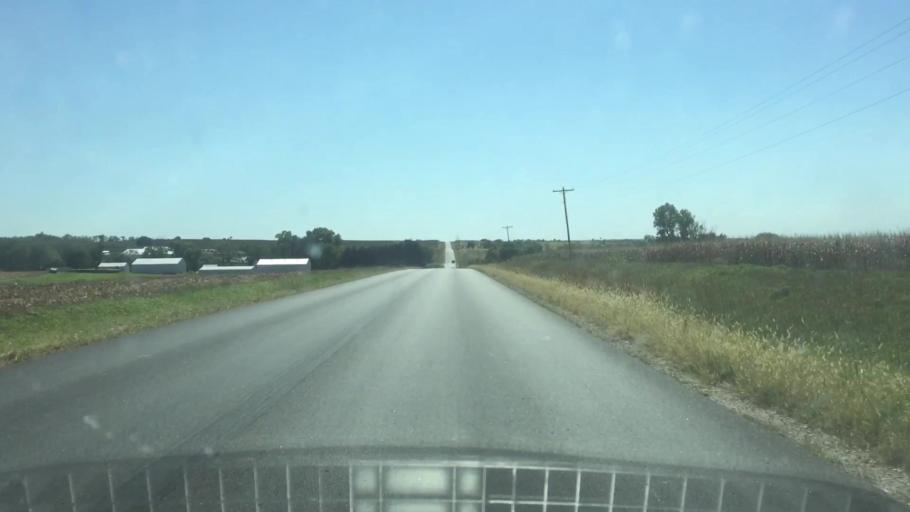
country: US
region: Kansas
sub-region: Marshall County
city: Marysville
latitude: 39.9049
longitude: -96.6010
